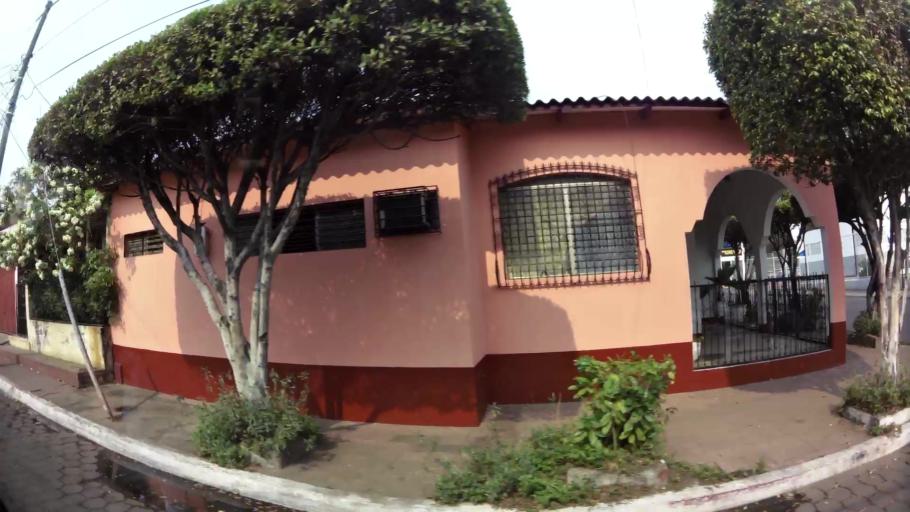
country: NI
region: Chinandega
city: Chinandega
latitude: 12.6304
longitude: -87.1231
